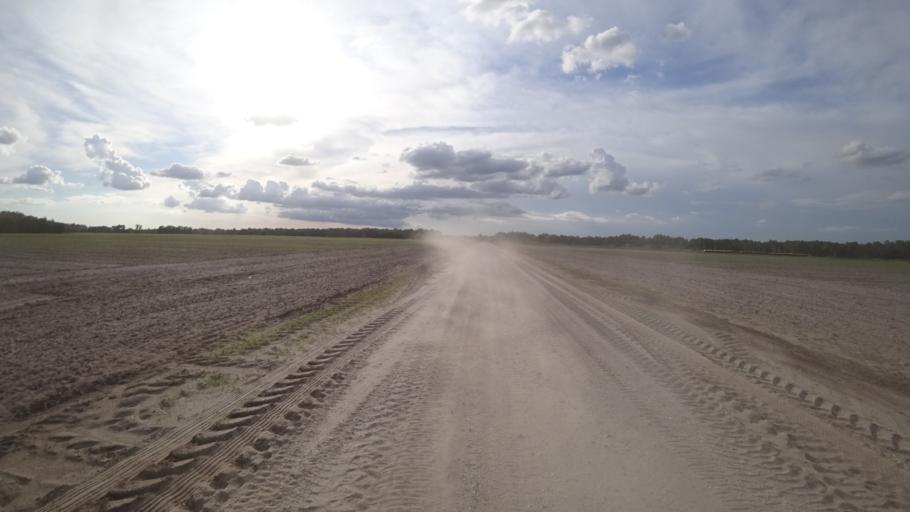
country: US
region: Florida
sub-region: Hardee County
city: Bowling Green
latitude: 27.5665
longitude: -82.0777
